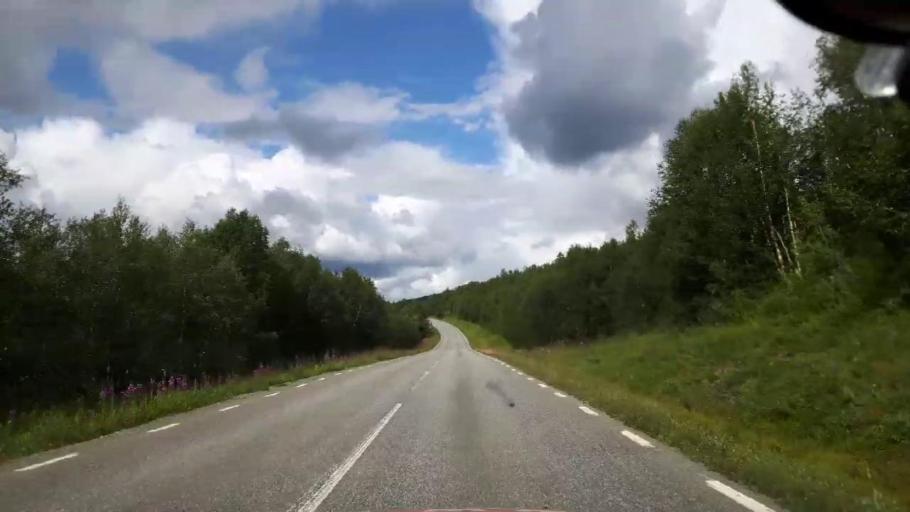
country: NO
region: Nordland
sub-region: Hattfjelldal
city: Hattfjelldal
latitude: 65.0520
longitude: 14.7401
